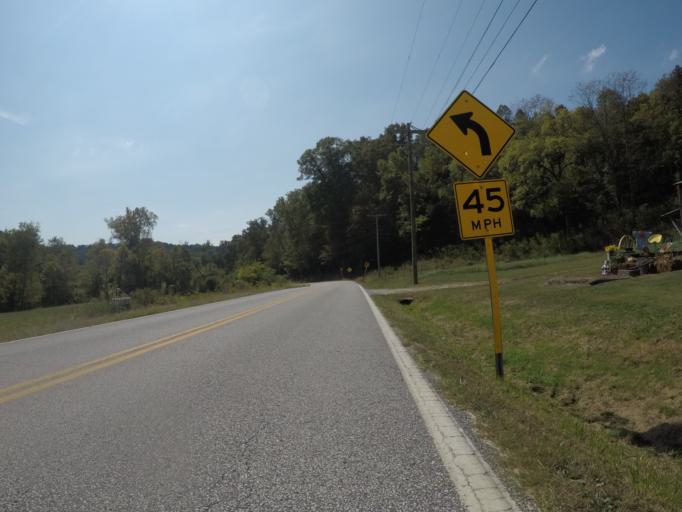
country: US
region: West Virginia
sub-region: Cabell County
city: Lesage
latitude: 38.5239
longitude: -82.3896
